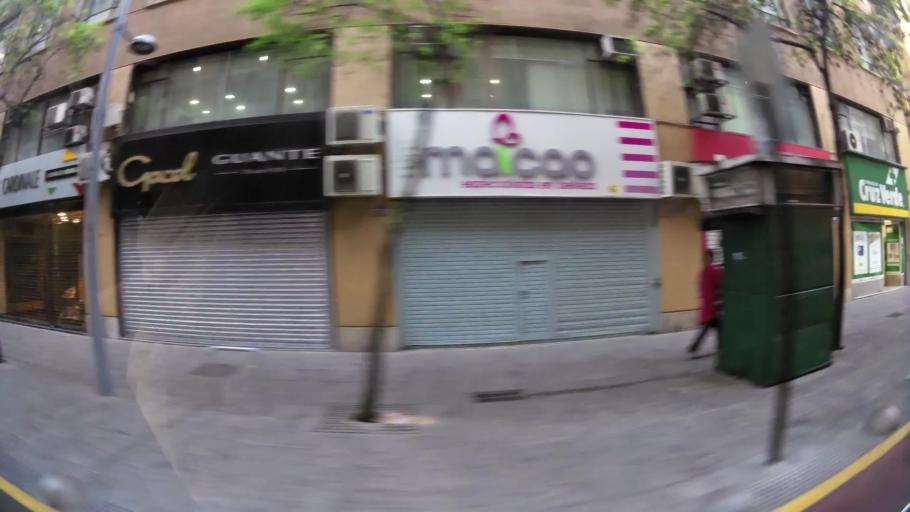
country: CL
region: Santiago Metropolitan
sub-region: Provincia de Santiago
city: Santiago
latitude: -33.4396
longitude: -70.6482
